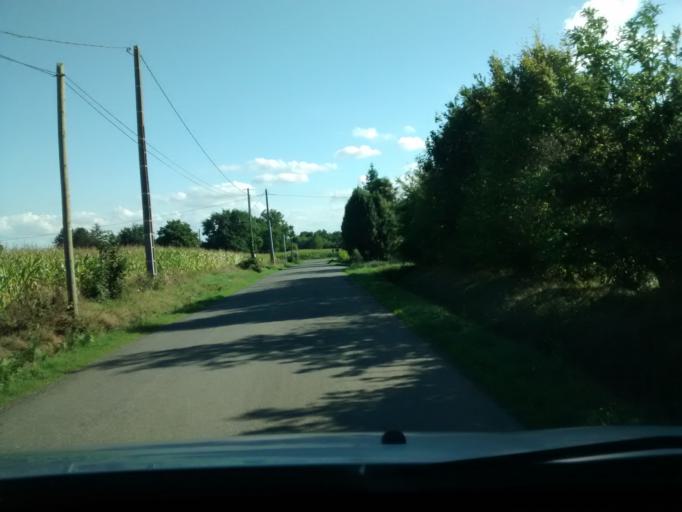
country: FR
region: Brittany
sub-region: Departement d'Ille-et-Vilaine
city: Vern-sur-Seiche
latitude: 48.0759
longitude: -1.5769
